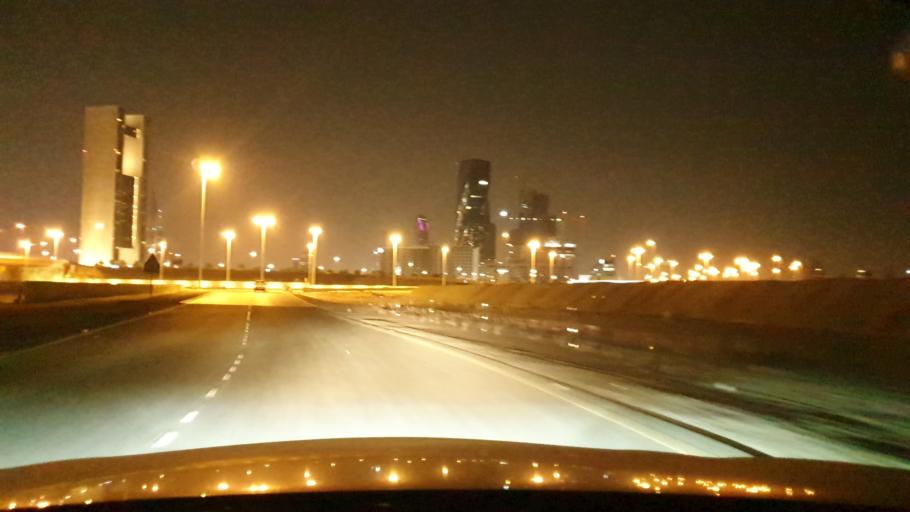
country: BH
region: Muharraq
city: Al Muharraq
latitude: 26.2550
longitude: 50.5814
